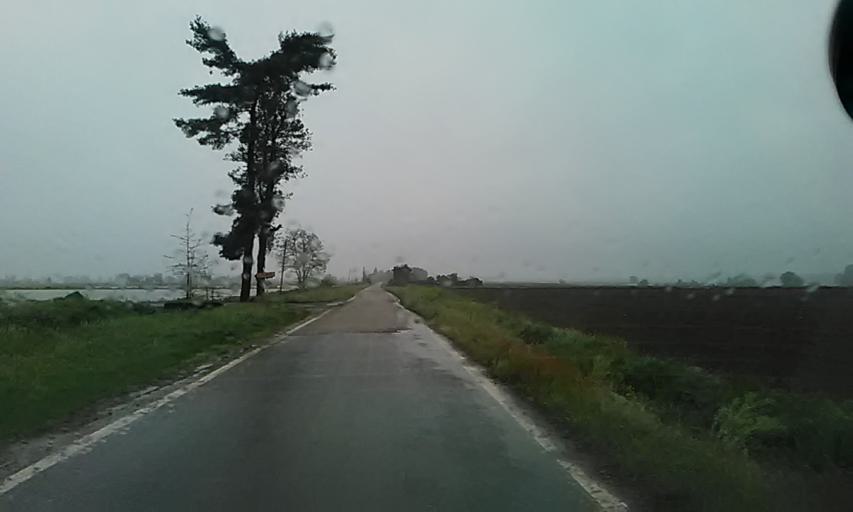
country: IT
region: Piedmont
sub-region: Provincia di Vercelli
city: San Giacomo Vercellese
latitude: 45.4799
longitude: 8.3384
